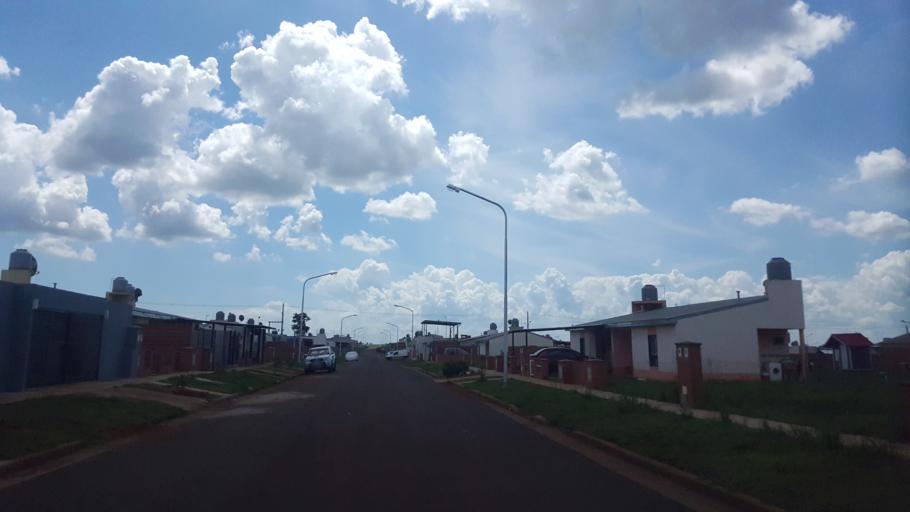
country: AR
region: Misiones
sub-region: Departamento de Capital
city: Posadas
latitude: -27.4061
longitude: -55.9793
